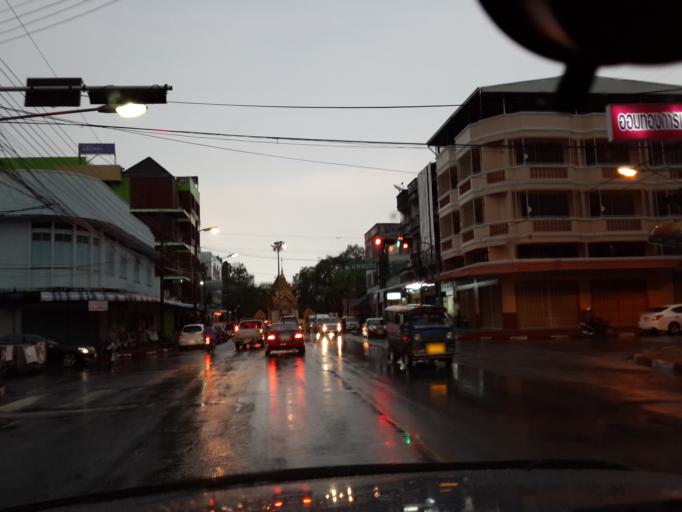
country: TH
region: Yala
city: Yala
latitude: 6.5574
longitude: 101.2894
